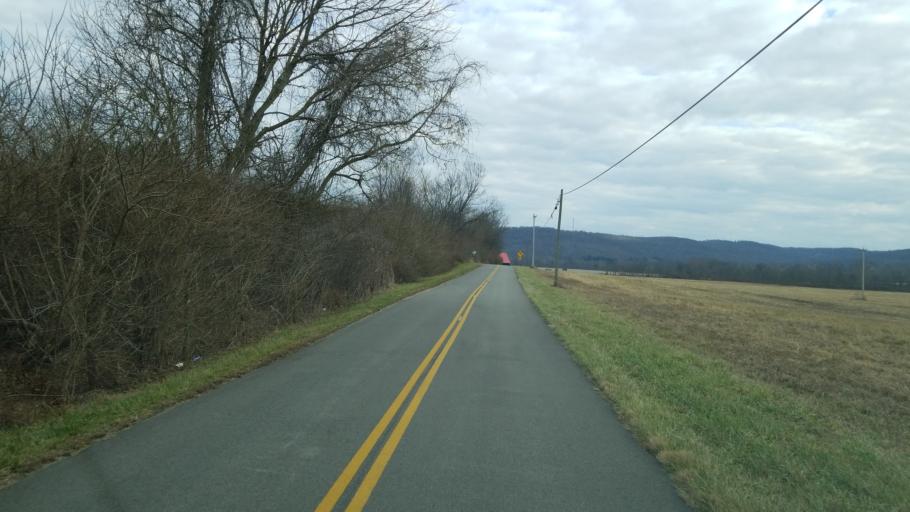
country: US
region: Ohio
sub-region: Highland County
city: Greenfield
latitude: 39.2283
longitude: -83.3089
